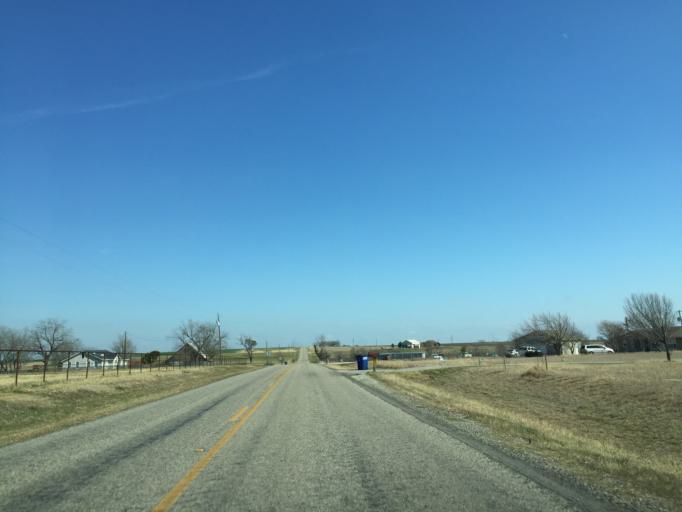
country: US
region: Texas
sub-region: Williamson County
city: Granger
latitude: 30.7537
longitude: -97.5442
